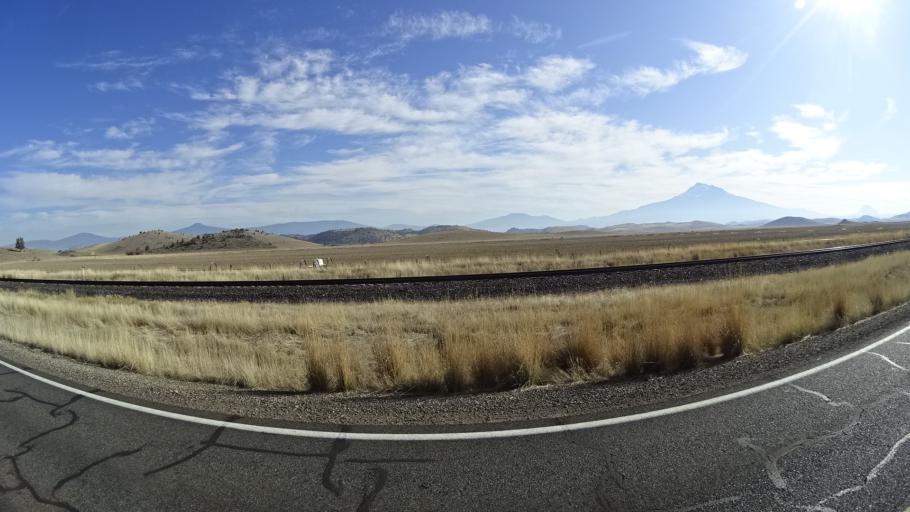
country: US
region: California
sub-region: Siskiyou County
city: Montague
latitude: 41.5791
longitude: -122.5247
